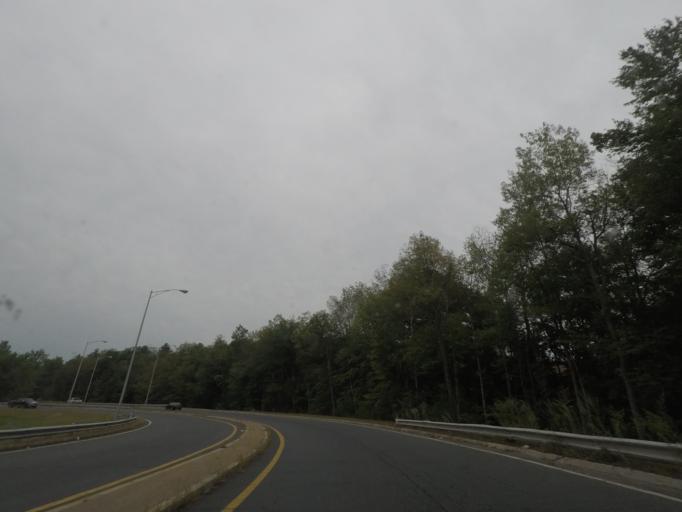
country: US
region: Massachusetts
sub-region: Hampden County
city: Palmer
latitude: 42.1737
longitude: -72.3331
